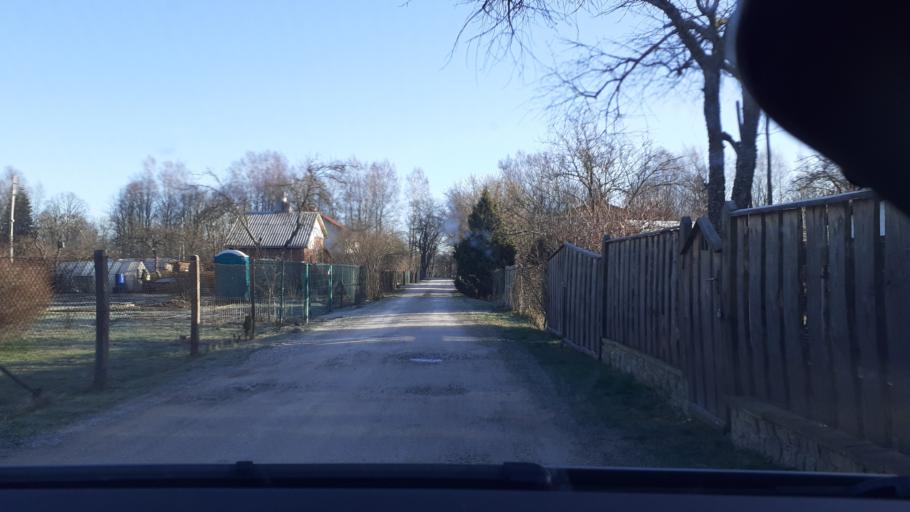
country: LV
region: Kuldigas Rajons
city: Kuldiga
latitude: 56.9530
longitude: 21.9992
